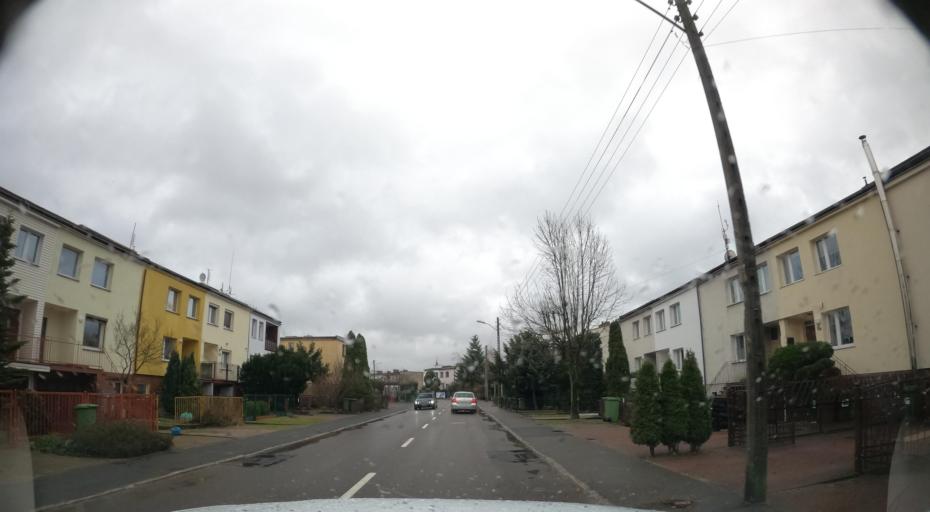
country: PL
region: West Pomeranian Voivodeship
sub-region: Szczecin
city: Szczecin
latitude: 53.3969
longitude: 14.6797
